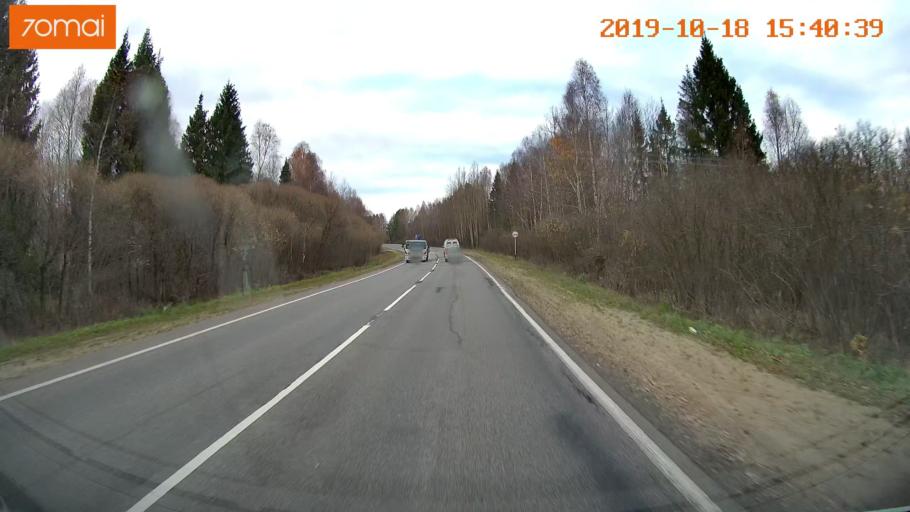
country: RU
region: Vladimir
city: Golovino
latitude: 55.9368
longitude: 40.5925
